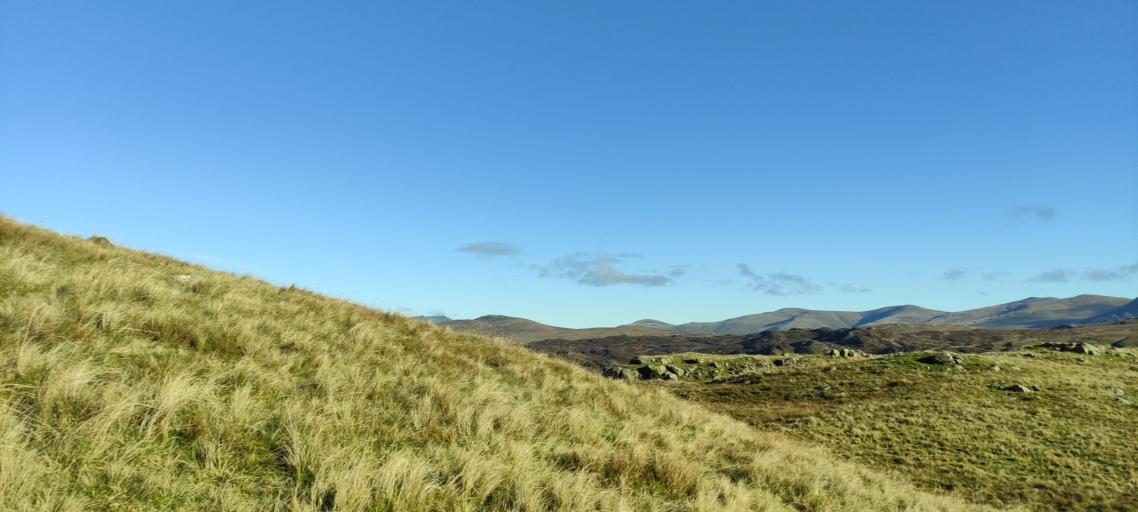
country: GB
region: England
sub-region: Cumbria
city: Keswick
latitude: 54.5044
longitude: -3.1421
